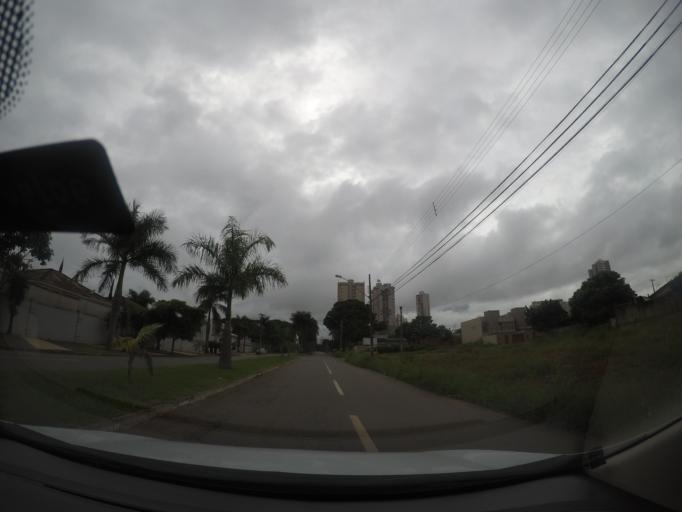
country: BR
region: Goias
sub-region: Goiania
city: Goiania
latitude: -16.7291
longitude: -49.2875
